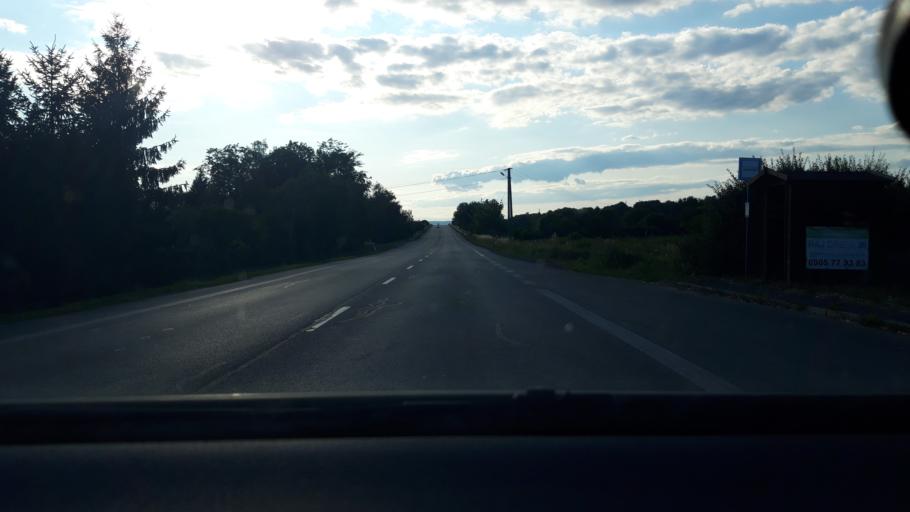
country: SK
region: Banskobystricky
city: Lucenec
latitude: 48.3055
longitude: 19.7228
